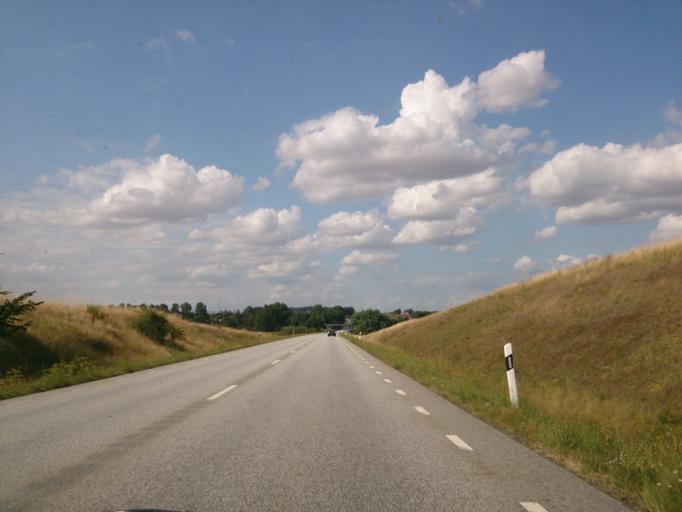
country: SE
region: Skane
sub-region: Kavlinge Kommun
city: Kaevlinge
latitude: 55.7873
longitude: 13.1322
